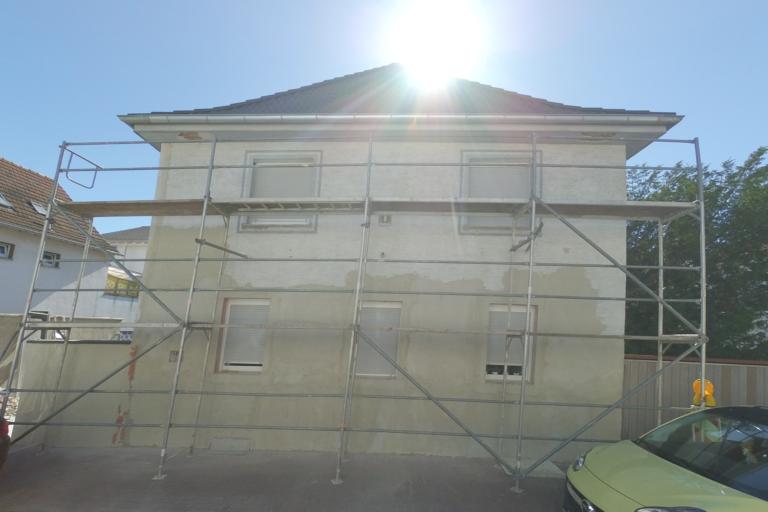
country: DE
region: Hesse
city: Viernheim
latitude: 49.5406
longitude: 8.5763
